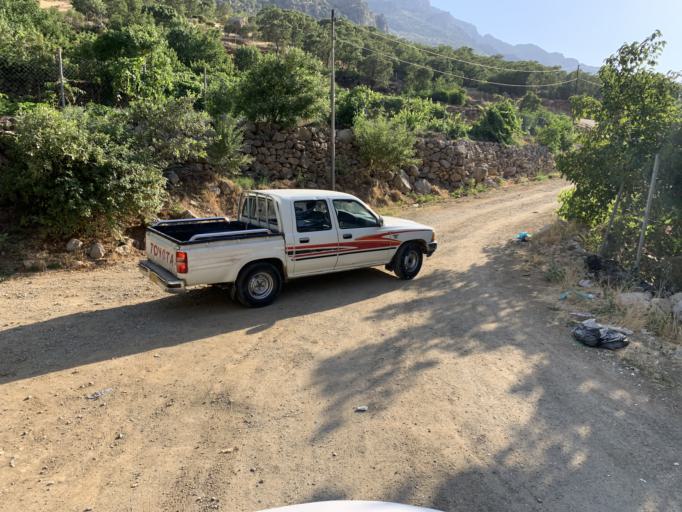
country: IQ
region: As Sulaymaniyah
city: Qeladize
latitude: 35.9885
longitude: 45.2001
